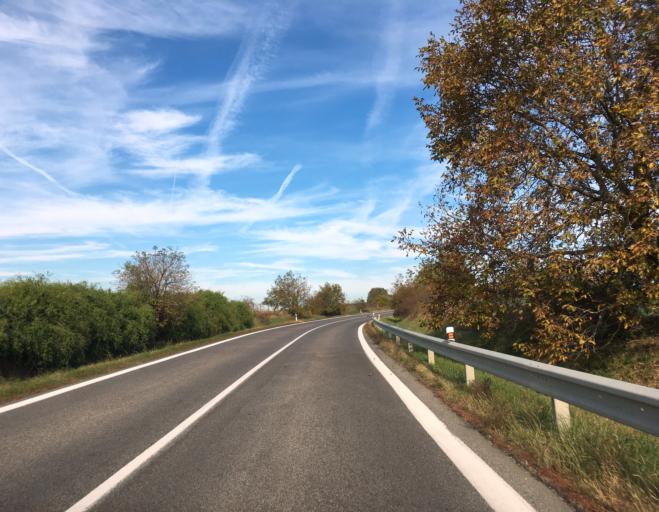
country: SK
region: Nitriansky
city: Svodin
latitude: 48.0230
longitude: 18.4206
